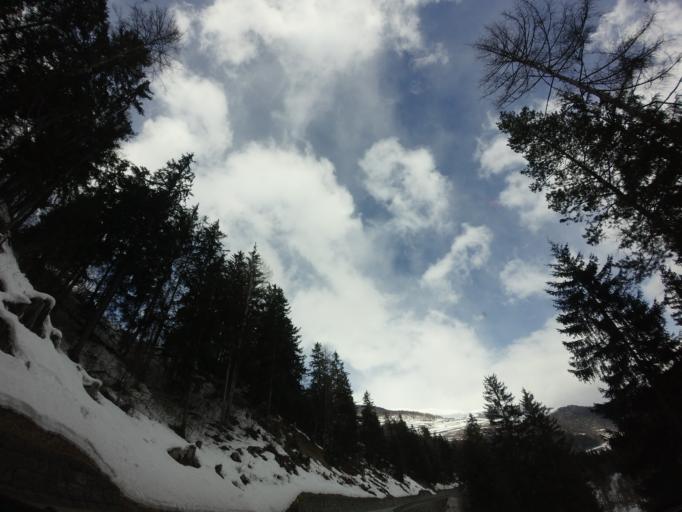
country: AT
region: Tyrol
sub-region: Politischer Bezirk Landeck
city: Nauders
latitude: 46.8499
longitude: 10.4207
